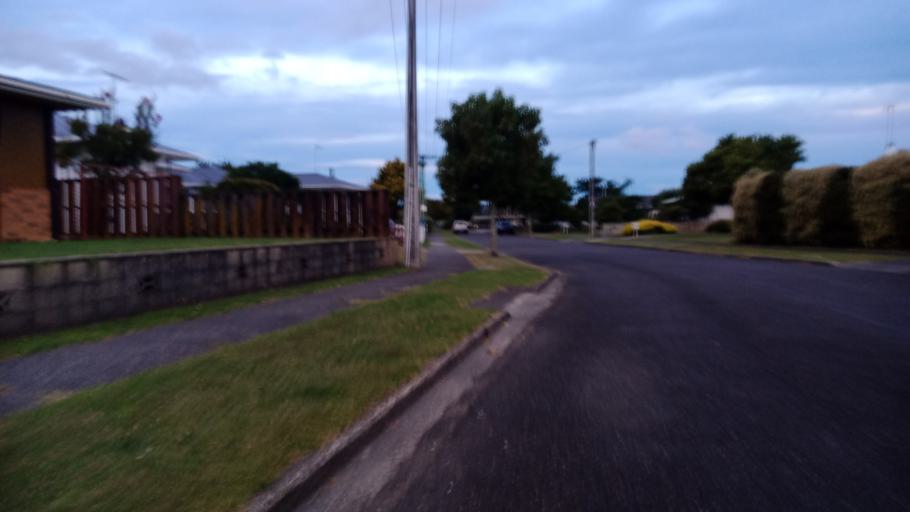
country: NZ
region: Gisborne
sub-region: Gisborne District
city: Gisborne
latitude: -38.6496
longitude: 177.9993
